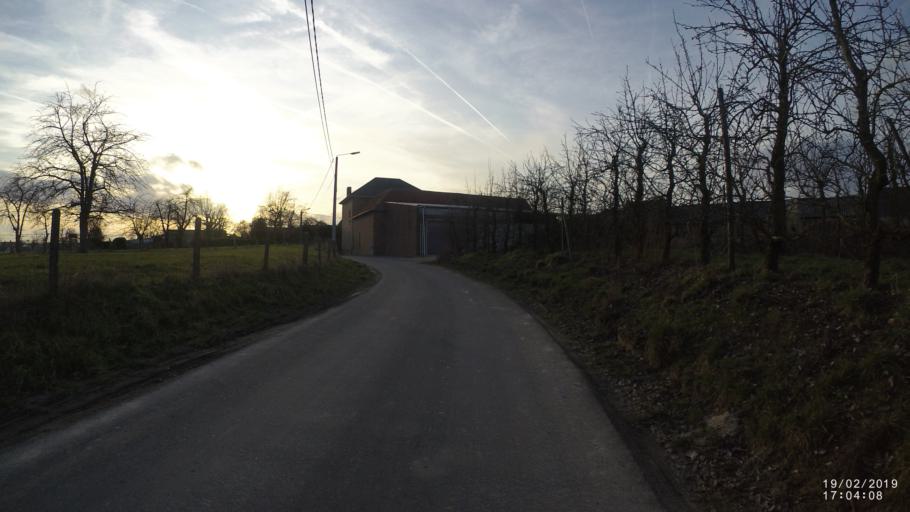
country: BE
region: Flanders
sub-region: Provincie Limburg
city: Borgloon
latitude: 50.8129
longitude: 5.2953
